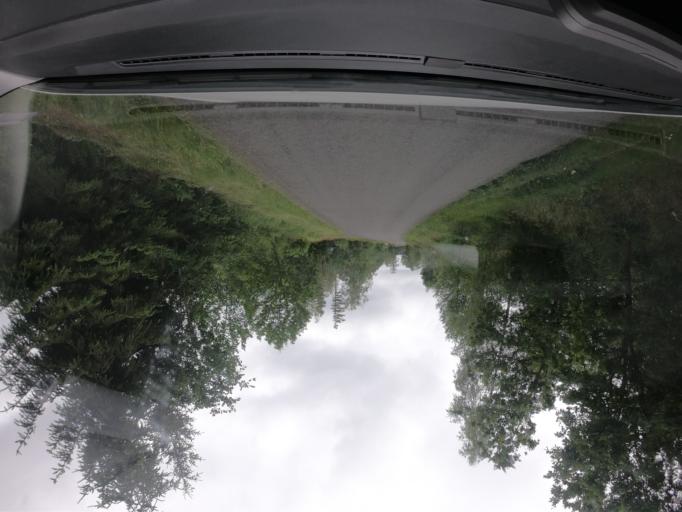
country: SE
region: Skane
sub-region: Perstorps Kommun
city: Perstorp
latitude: 56.1612
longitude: 13.5000
